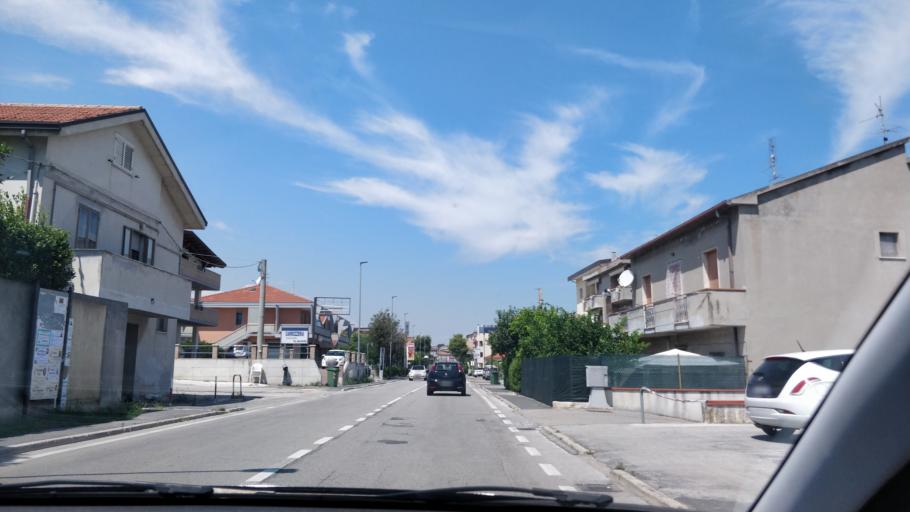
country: IT
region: Abruzzo
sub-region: Provincia di Chieti
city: Francavilla al Mare
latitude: 42.4122
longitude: 14.3024
